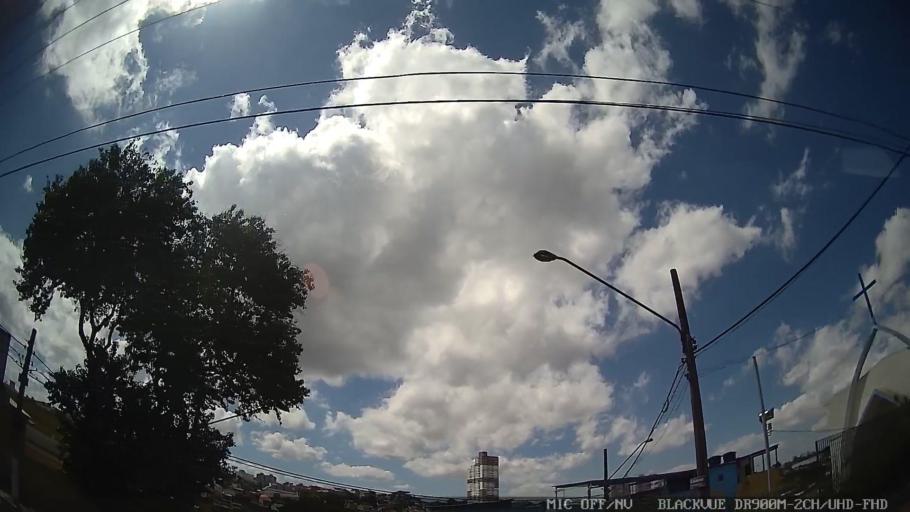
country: BR
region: Sao Paulo
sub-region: Diadema
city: Diadema
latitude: -23.6656
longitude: -46.6022
